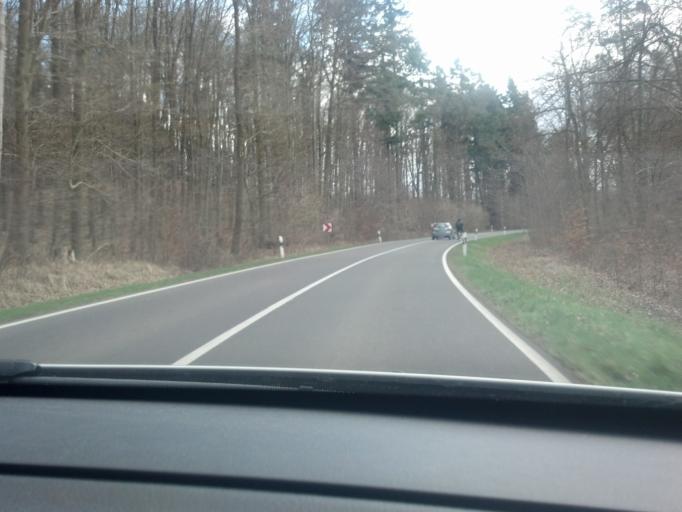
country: DE
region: Mecklenburg-Vorpommern
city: Loitz
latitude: 53.3620
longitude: 13.3988
